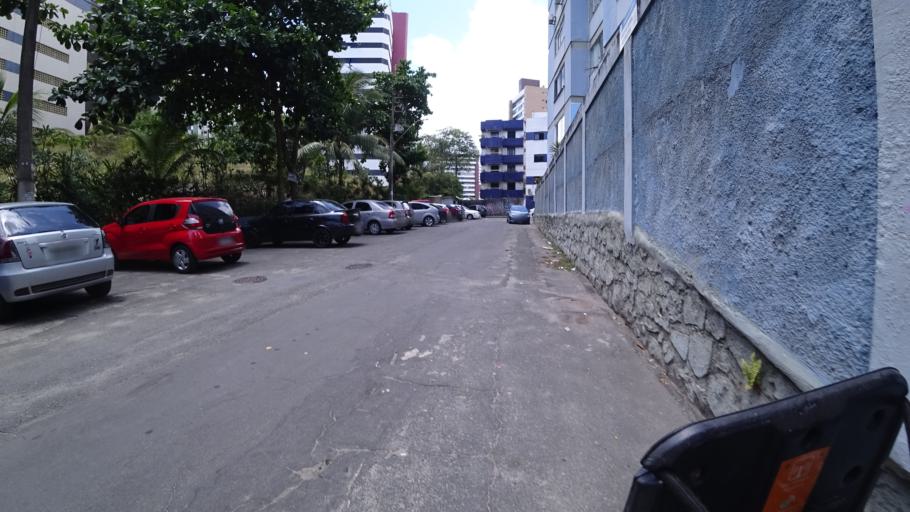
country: BR
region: Bahia
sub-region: Salvador
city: Salvador
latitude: -13.0025
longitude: -38.4615
